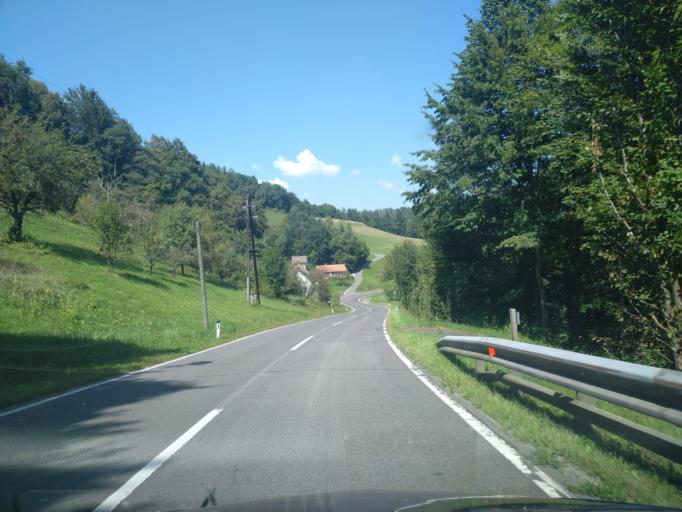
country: AT
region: Styria
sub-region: Politischer Bezirk Leibnitz
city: Leutschach
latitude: 46.6914
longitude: 15.4890
